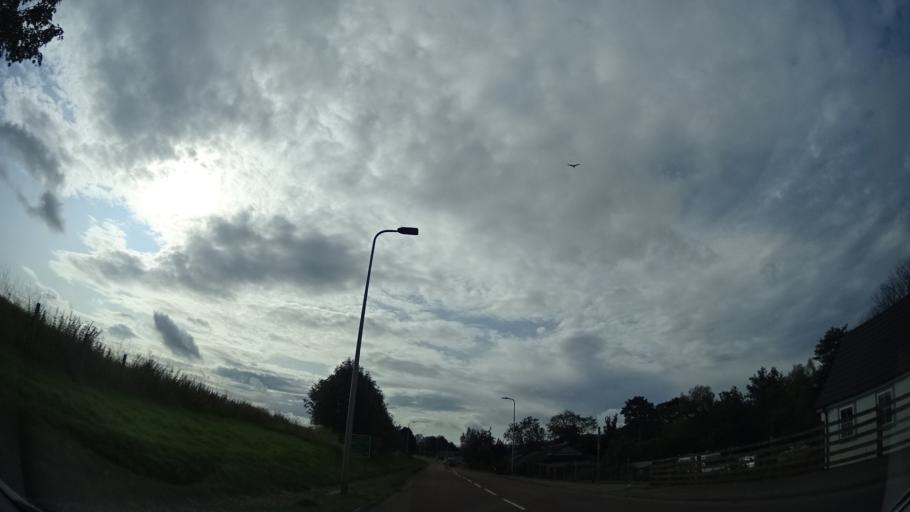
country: GB
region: Scotland
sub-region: Highland
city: Muir of Ord
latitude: 57.5651
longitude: -4.5780
